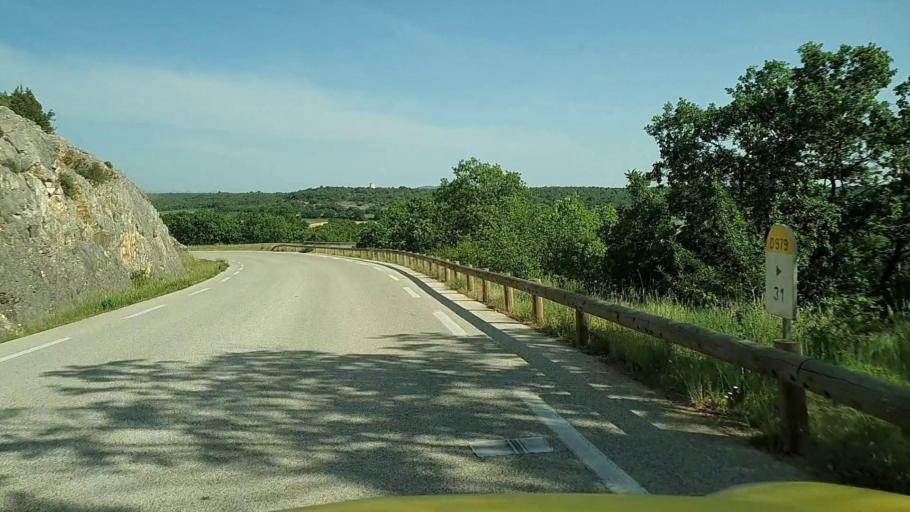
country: FR
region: Languedoc-Roussillon
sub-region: Departement du Gard
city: Montaren-et-Saint-Mediers
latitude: 44.1257
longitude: 4.3651
